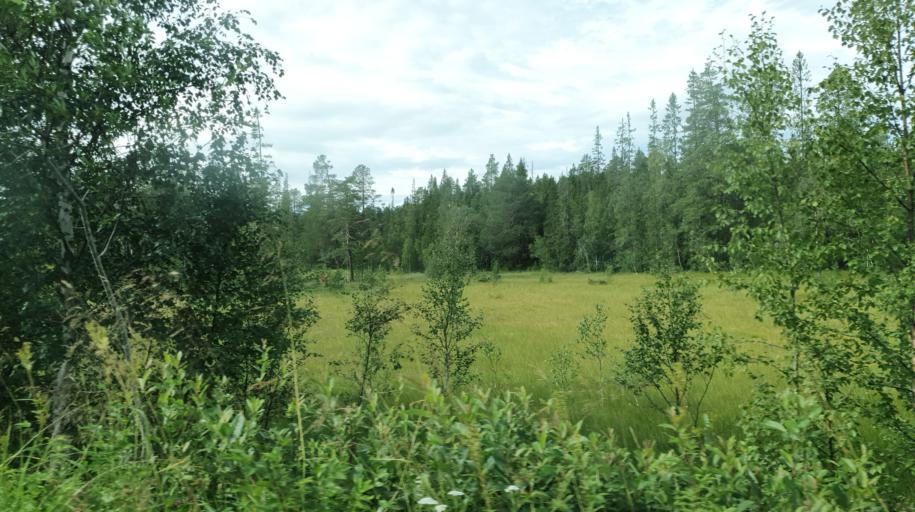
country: NO
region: Nord-Trondelag
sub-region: Levanger
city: Skogn
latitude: 63.5771
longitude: 11.2400
